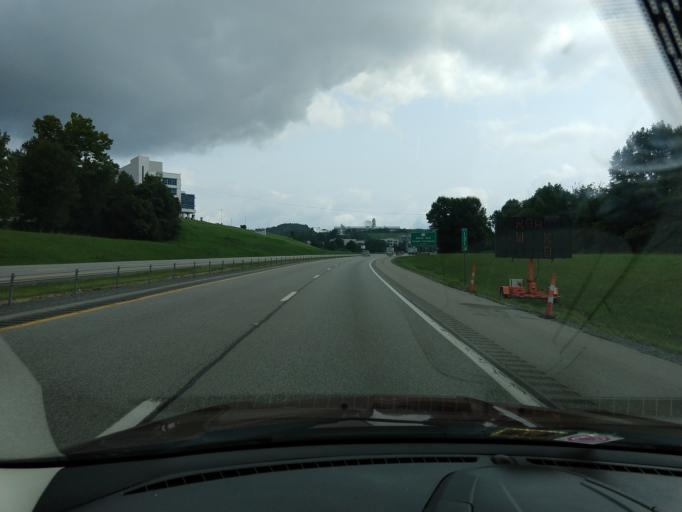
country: US
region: West Virginia
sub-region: Marion County
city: Monongah
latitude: 39.4257
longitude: -80.1972
